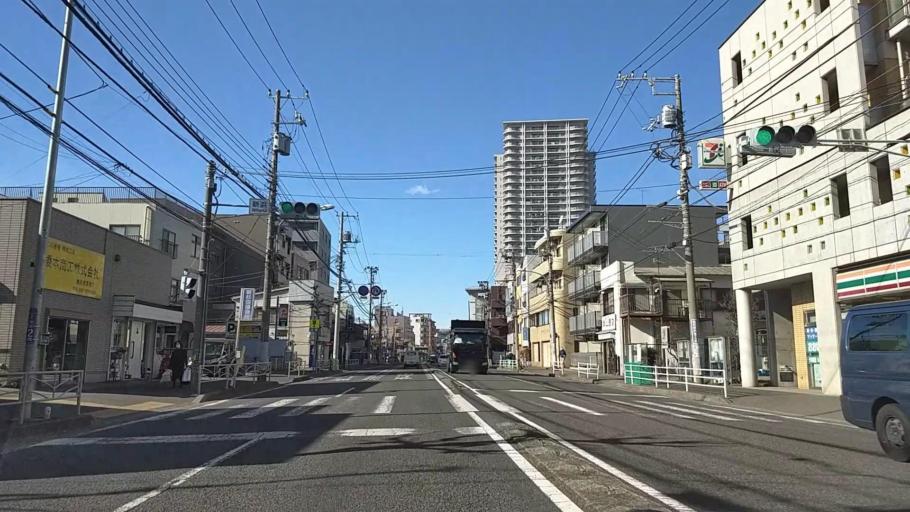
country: JP
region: Kanagawa
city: Yokohama
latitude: 35.3835
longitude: 139.6205
